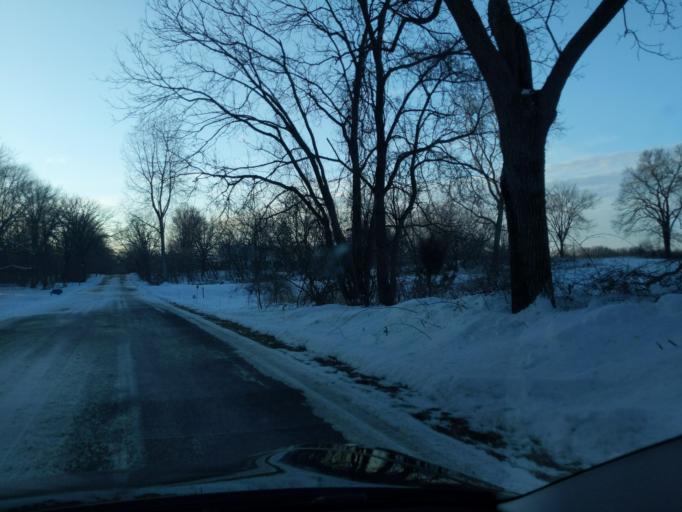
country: US
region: Michigan
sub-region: Ingham County
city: Webberville
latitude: 42.5687
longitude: -84.1574
